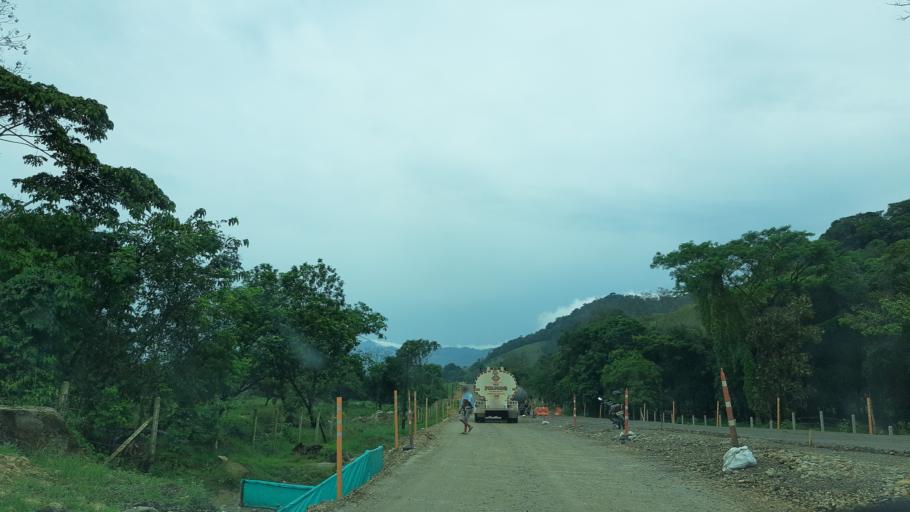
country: CO
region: Casanare
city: Sabanalarga
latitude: 4.8217
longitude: -72.9684
